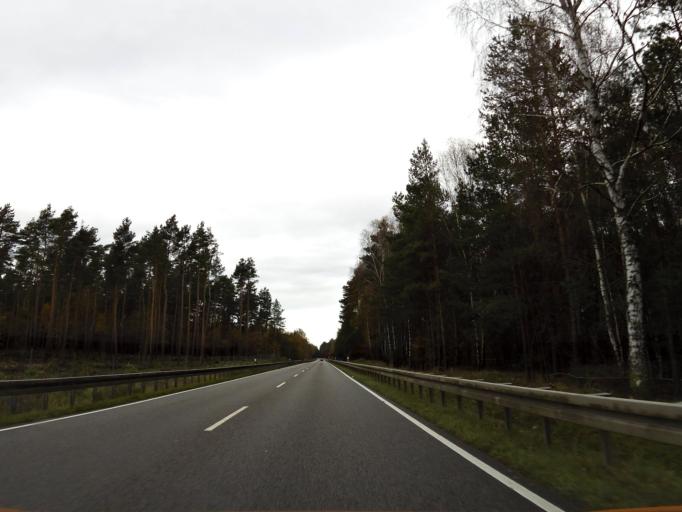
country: DE
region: Saxony-Anhalt
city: Colbitz
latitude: 52.3459
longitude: 11.5740
